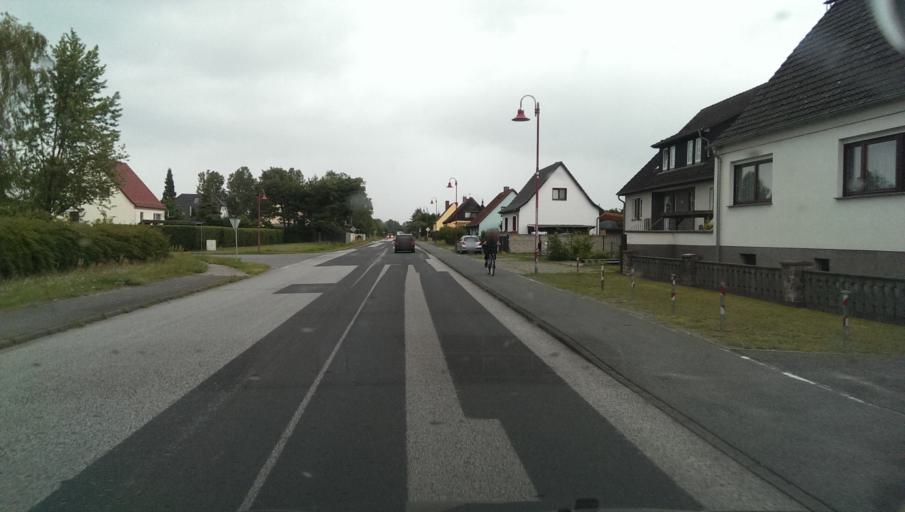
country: DE
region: Brandenburg
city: Premnitz
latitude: 52.5217
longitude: 12.3676
